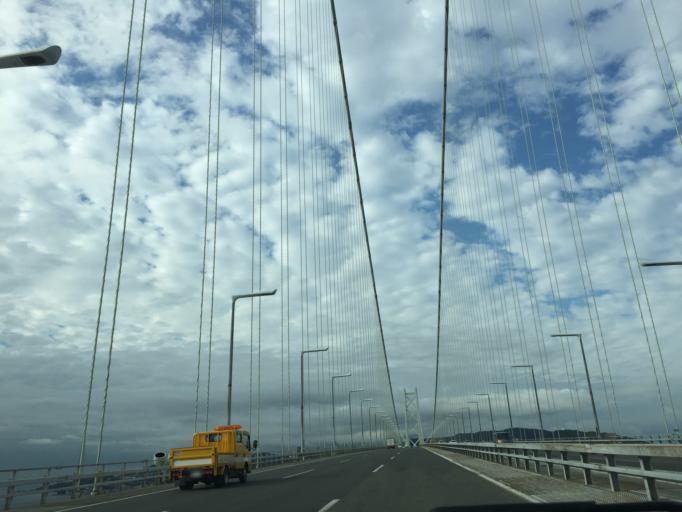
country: JP
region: Hyogo
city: Akashi
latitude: 34.6237
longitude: 135.0270
